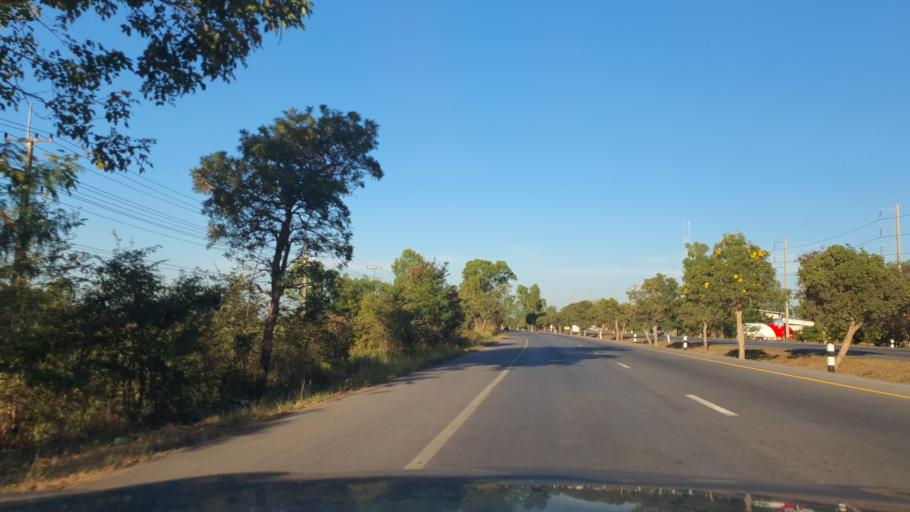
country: TH
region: Phitsanulok
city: Phitsanulok
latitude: 16.8632
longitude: 100.2962
